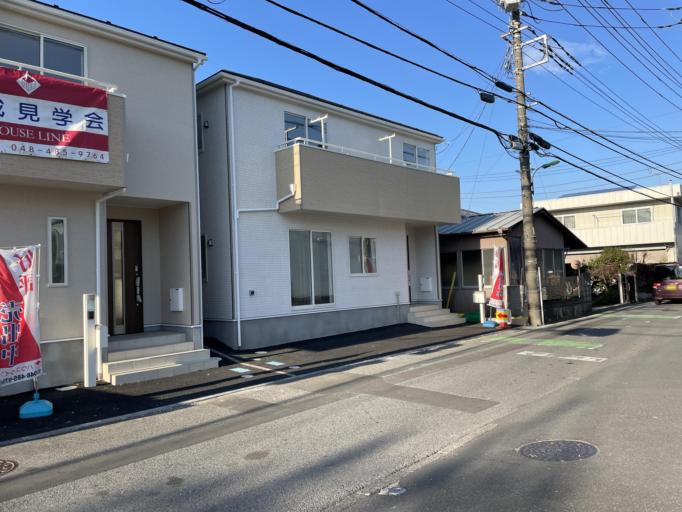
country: JP
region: Saitama
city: Asaka
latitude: 35.7912
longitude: 139.5827
